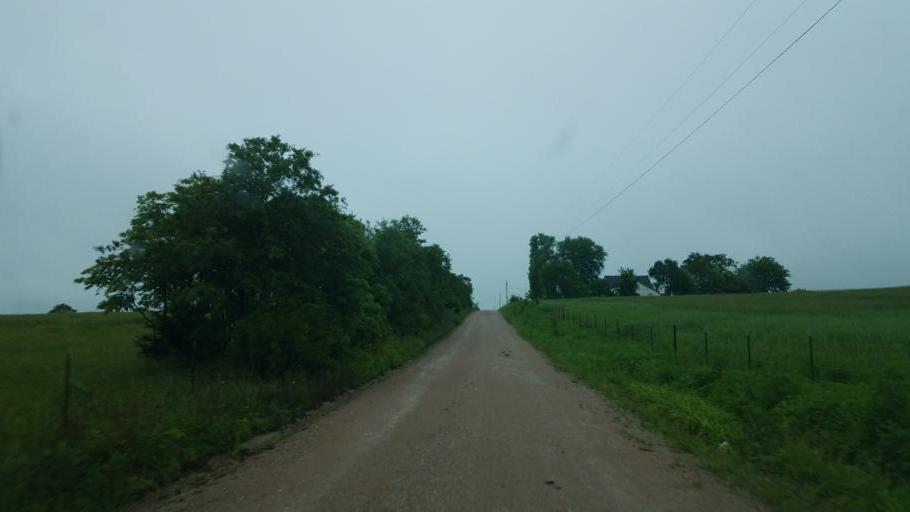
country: US
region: Missouri
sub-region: Moniteau County
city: California
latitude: 38.7509
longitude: -92.6057
